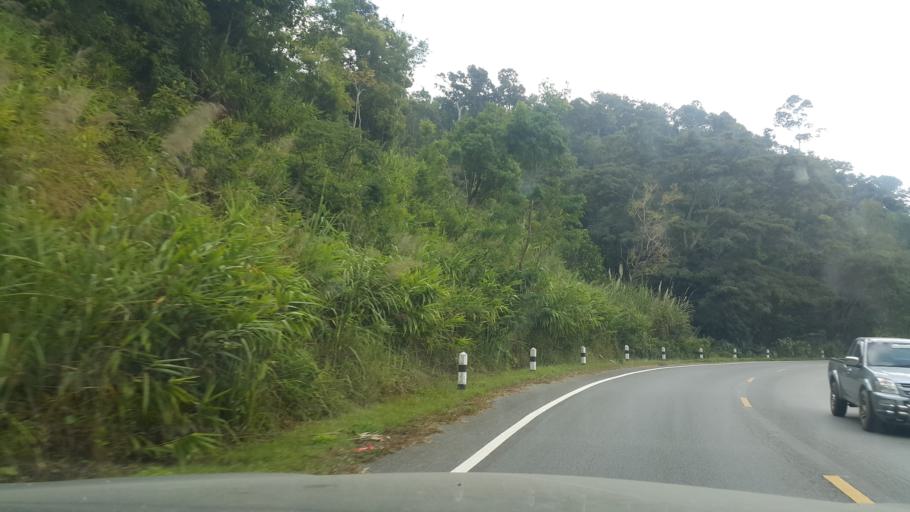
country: TH
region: Phayao
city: Phayao
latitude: 19.0702
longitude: 99.7728
